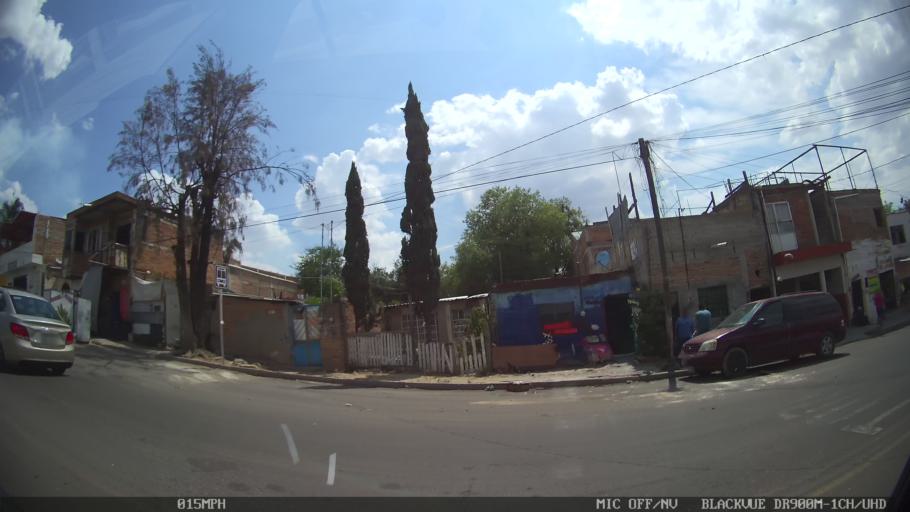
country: MX
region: Jalisco
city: Tonala
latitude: 20.6211
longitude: -103.2528
